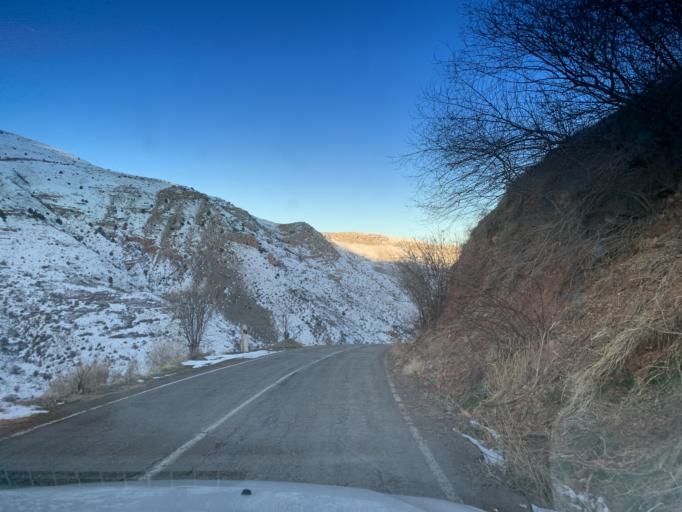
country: AM
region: Vayots' Dzori Marz
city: Areni
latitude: 39.6839
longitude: 45.2332
